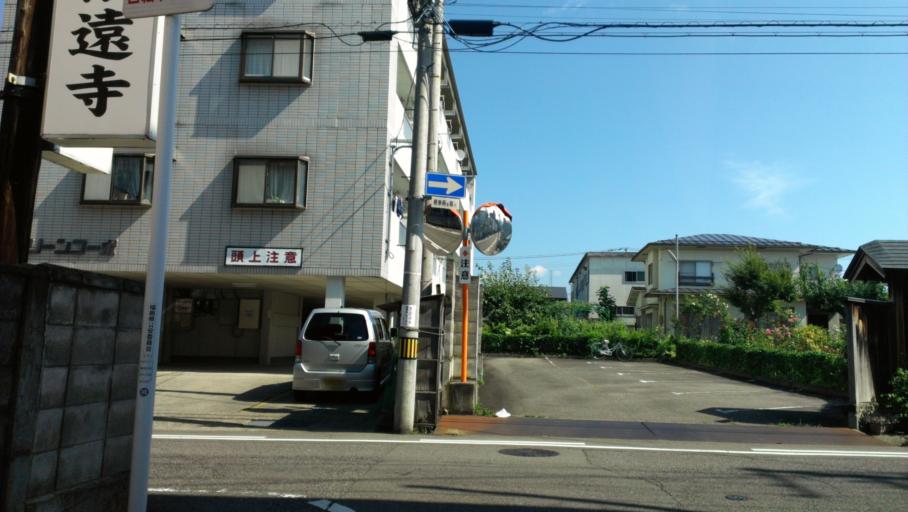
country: JP
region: Fukushima
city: Kitakata
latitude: 37.4984
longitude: 139.9221
